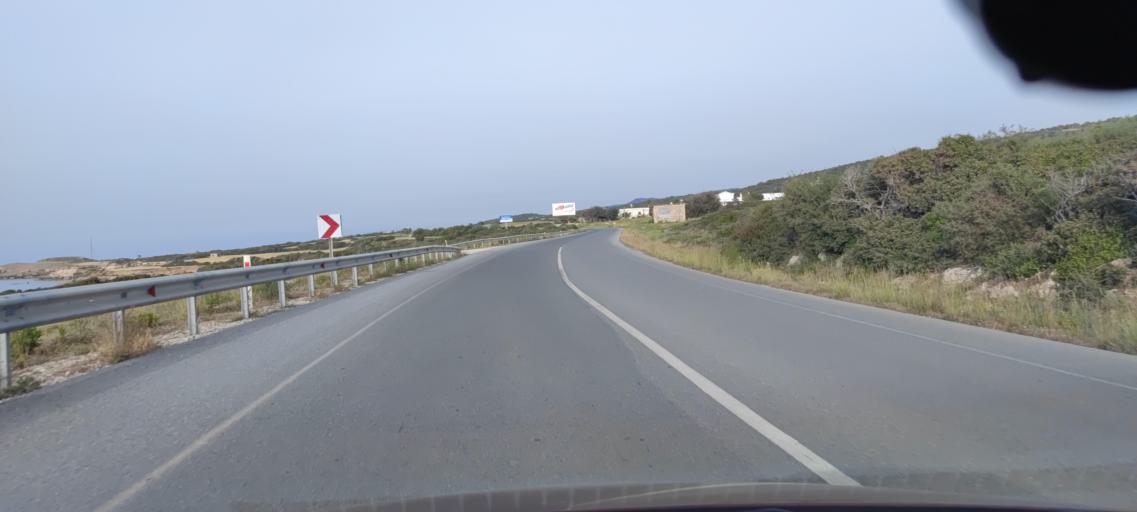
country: CY
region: Ammochostos
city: Leonarisso
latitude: 35.5583
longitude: 34.2356
